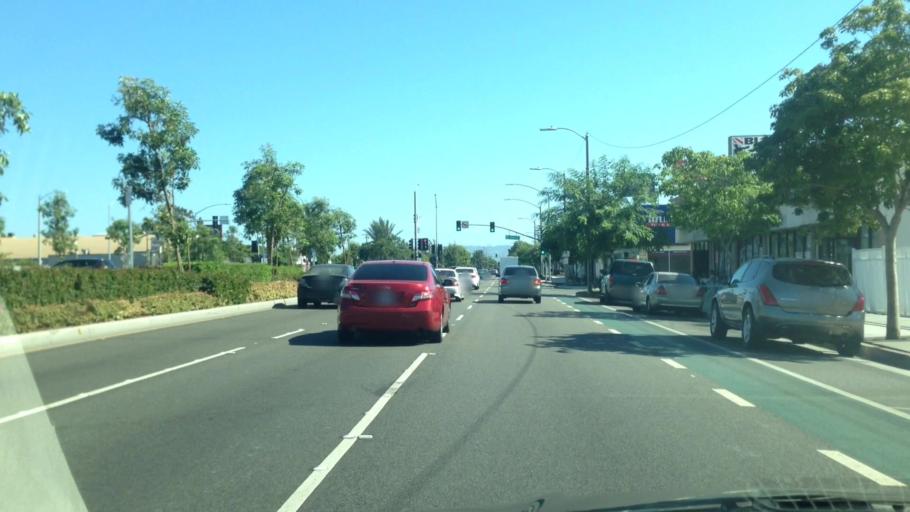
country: US
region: California
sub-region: Los Angeles County
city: Hawthorne
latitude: 33.9052
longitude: -118.3528
